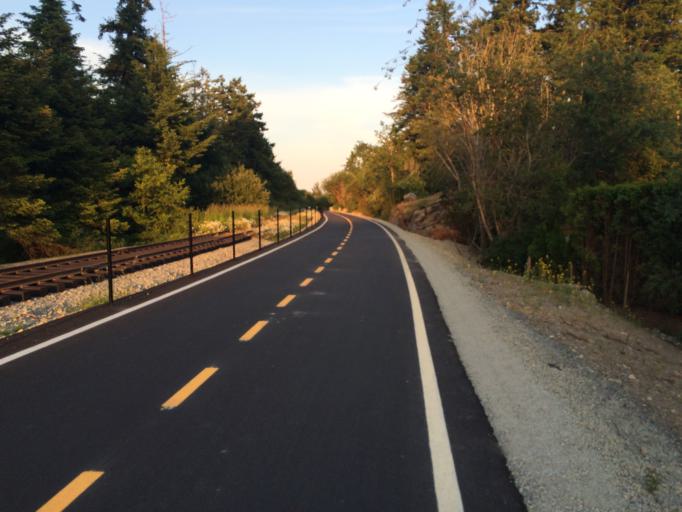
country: CA
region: British Columbia
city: Colwood
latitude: 48.4594
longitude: -123.4415
